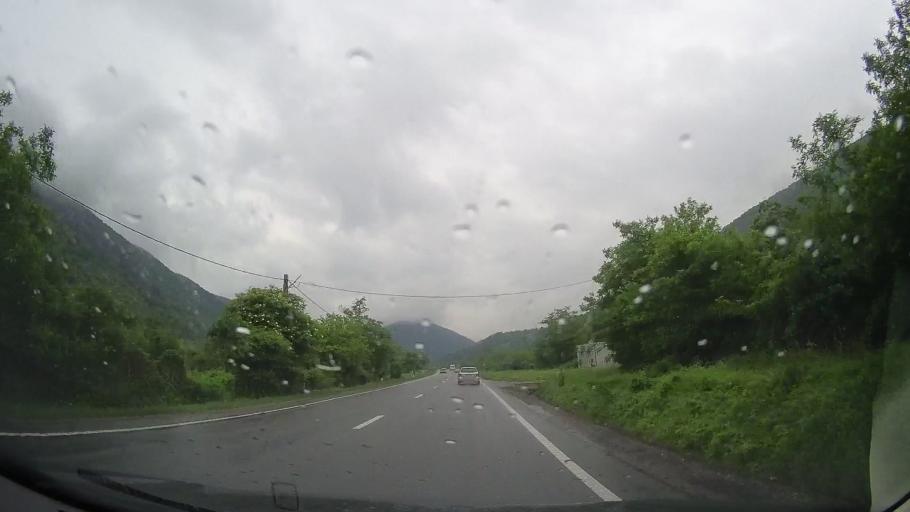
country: RO
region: Caras-Severin
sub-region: Comuna Mehadia
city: Mehadia
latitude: 44.8793
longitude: 22.3840
